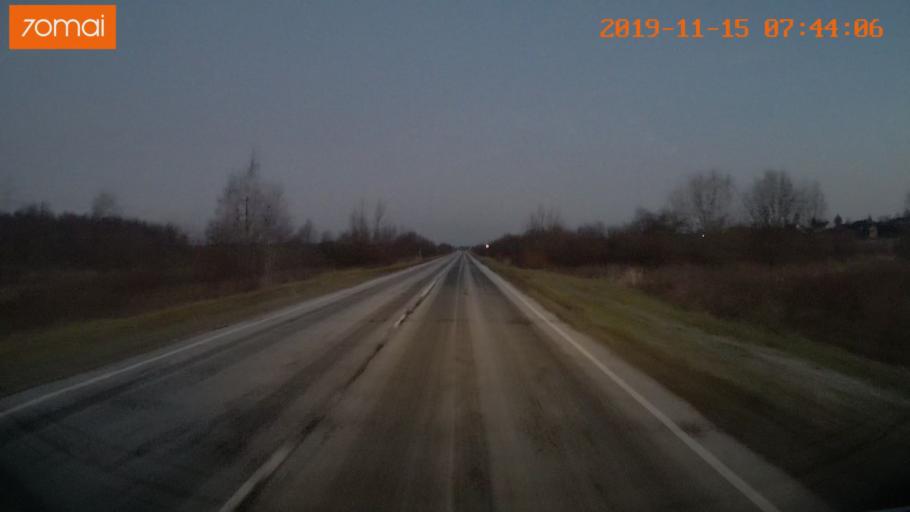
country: RU
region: Vologda
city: Sheksna
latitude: 58.8078
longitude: 38.3207
